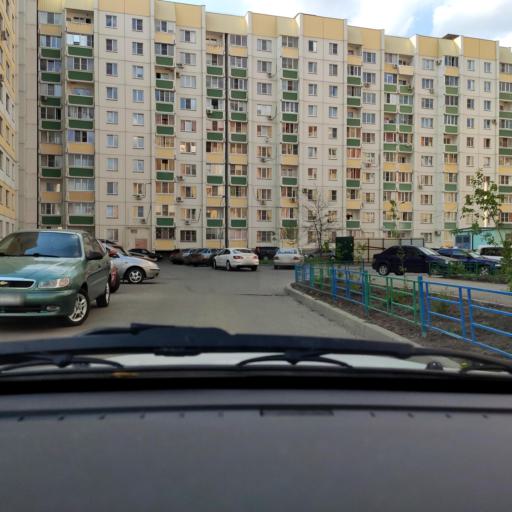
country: RU
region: Voronezj
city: Pridonskoy
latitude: 51.6212
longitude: 39.0621
